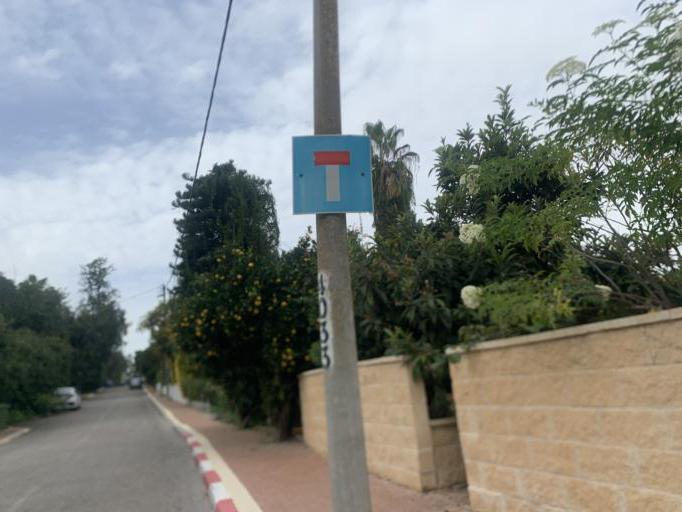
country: IL
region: Central District
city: Hod HaSharon
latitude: 32.1667
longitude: 34.8835
